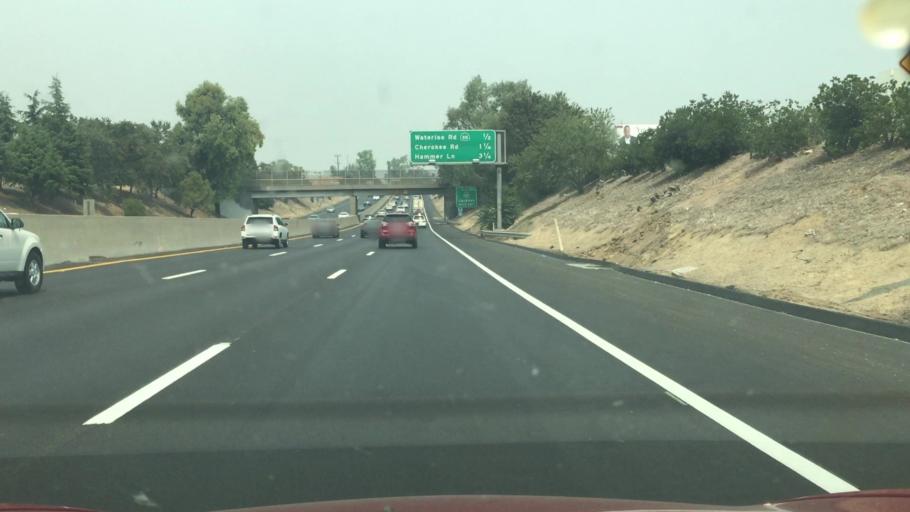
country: US
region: California
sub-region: San Joaquin County
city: August
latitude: 37.9747
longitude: -121.2477
